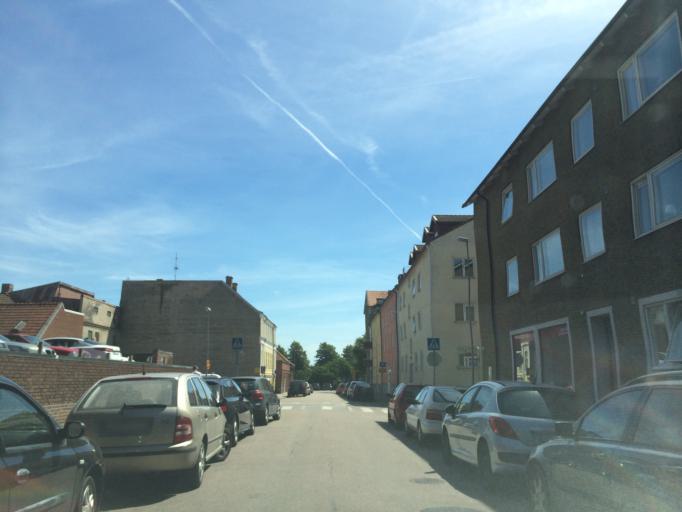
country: SE
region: Skane
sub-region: Landskrona
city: Landskrona
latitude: 55.8683
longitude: 12.8283
